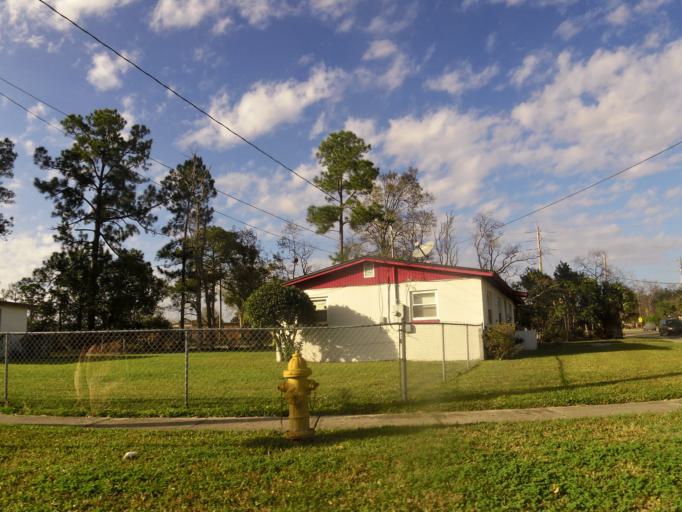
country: US
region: Florida
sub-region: Duval County
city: Jacksonville
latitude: 30.2765
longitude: -81.6102
